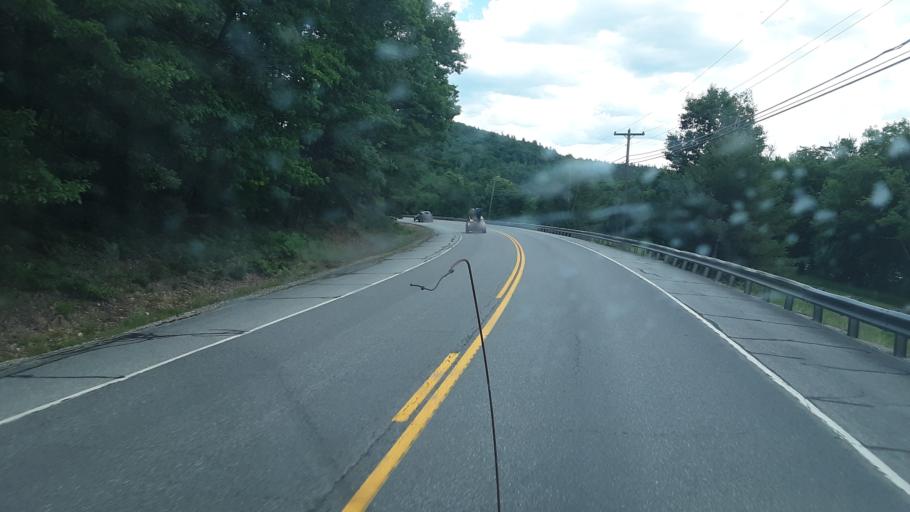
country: US
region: Maine
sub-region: Oxford County
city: Rumford
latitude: 44.4888
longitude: -70.6487
